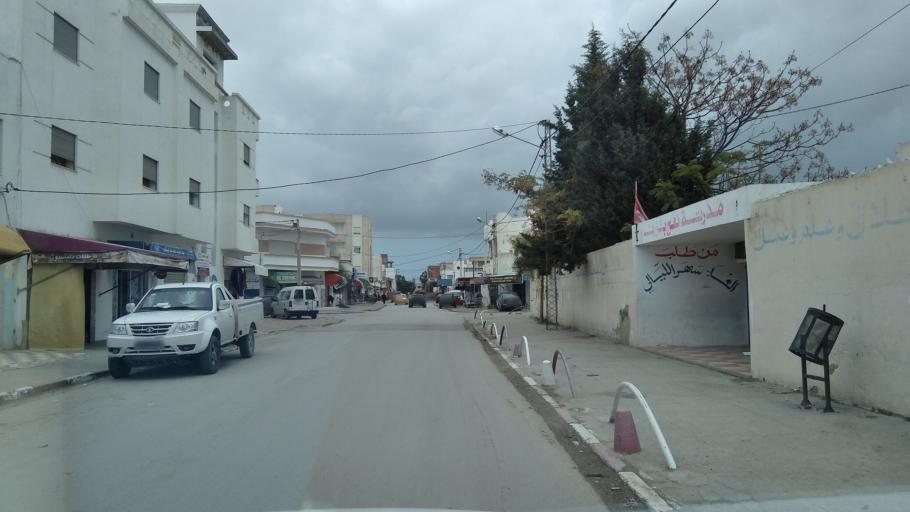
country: TN
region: Bin 'Arus
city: Ben Arous
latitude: 36.7602
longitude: 10.2265
